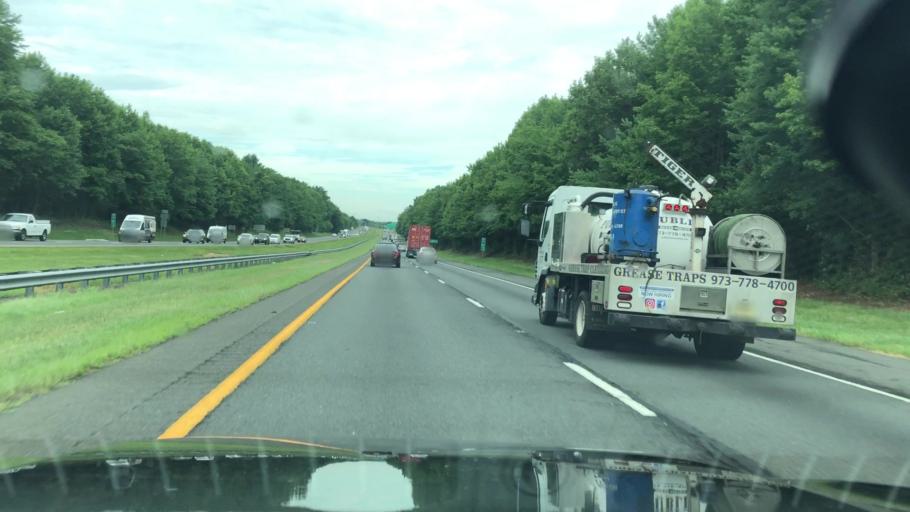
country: US
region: New Jersey
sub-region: Mercer County
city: Robbinsville
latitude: 40.1996
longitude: -74.6217
